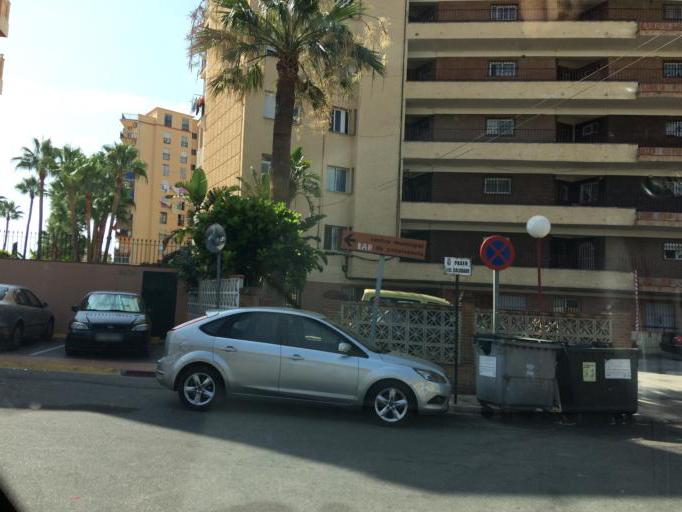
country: ES
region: Andalusia
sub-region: Provincia de Malaga
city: Torremolinos
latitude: 36.6339
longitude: -4.4901
